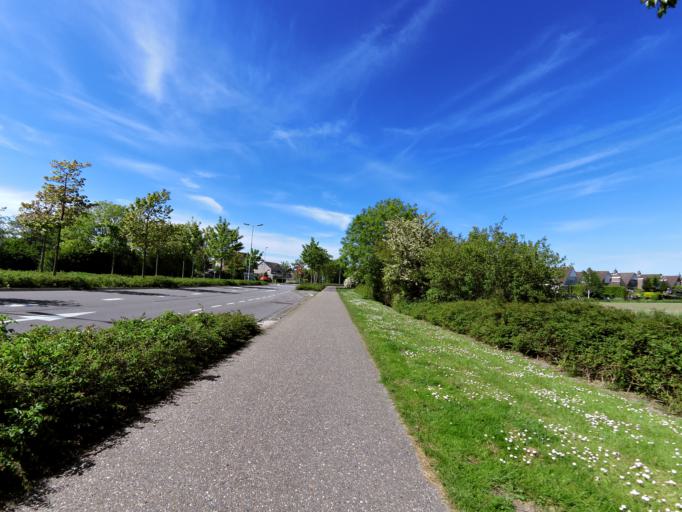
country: NL
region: South Holland
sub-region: Gemeente Hellevoetsluis
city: Nieuwenhoorn
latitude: 51.8387
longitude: 4.1557
